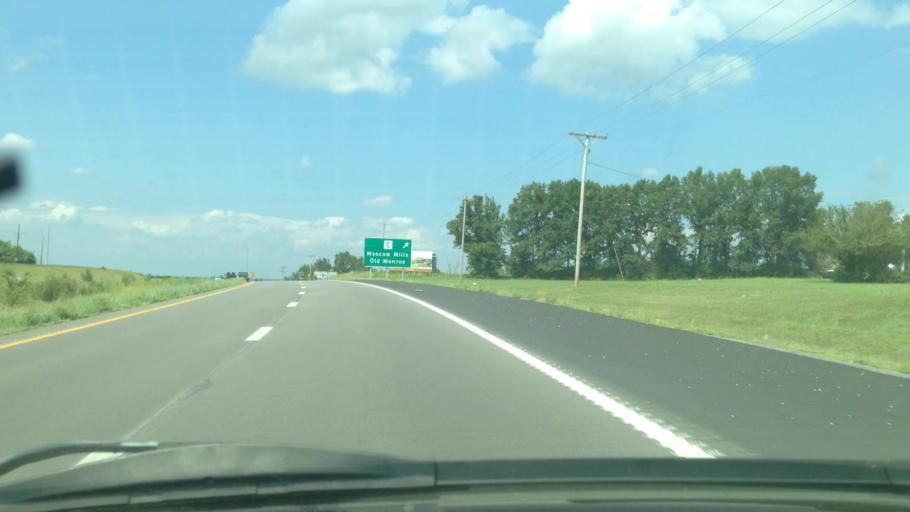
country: US
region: Missouri
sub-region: Lincoln County
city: Moscow Mills
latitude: 38.9396
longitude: -90.9255
